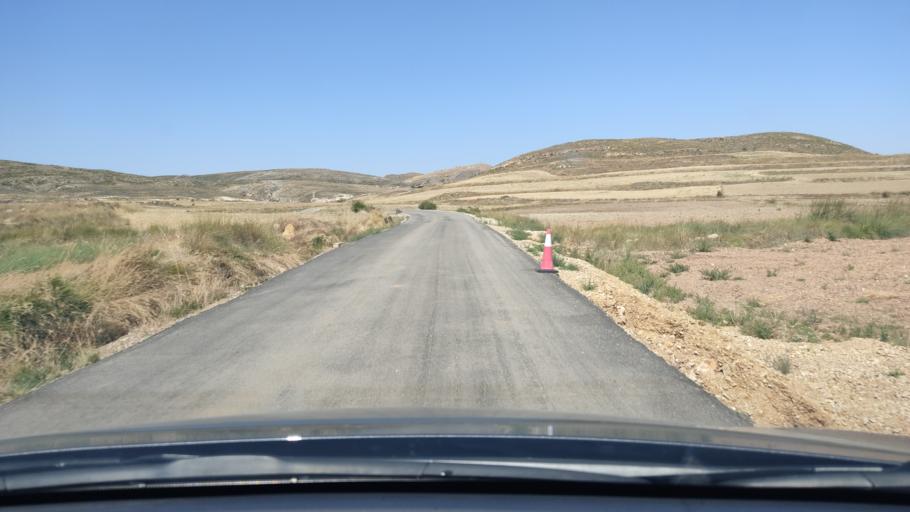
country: ES
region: Aragon
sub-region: Provincia de Teruel
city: Monforte de Moyuela
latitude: 41.0442
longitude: -0.9986
